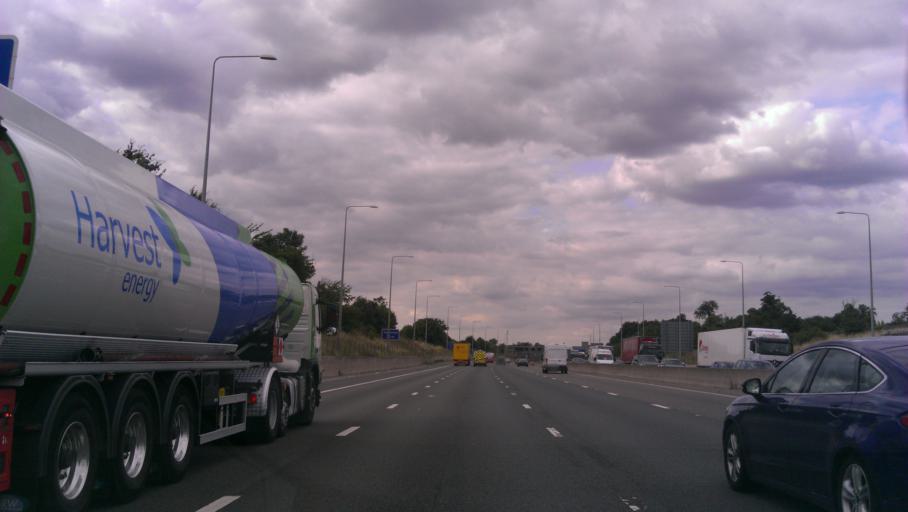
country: GB
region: England
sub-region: Essex
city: South Ockendon
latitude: 51.5072
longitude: 0.2674
